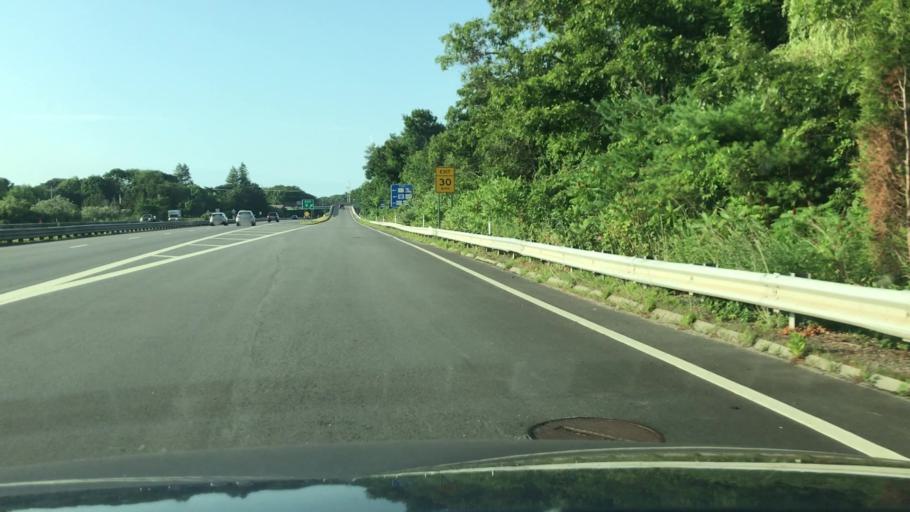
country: US
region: Massachusetts
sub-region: Plymouth County
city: Kingston
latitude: 41.9920
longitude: -70.7188
